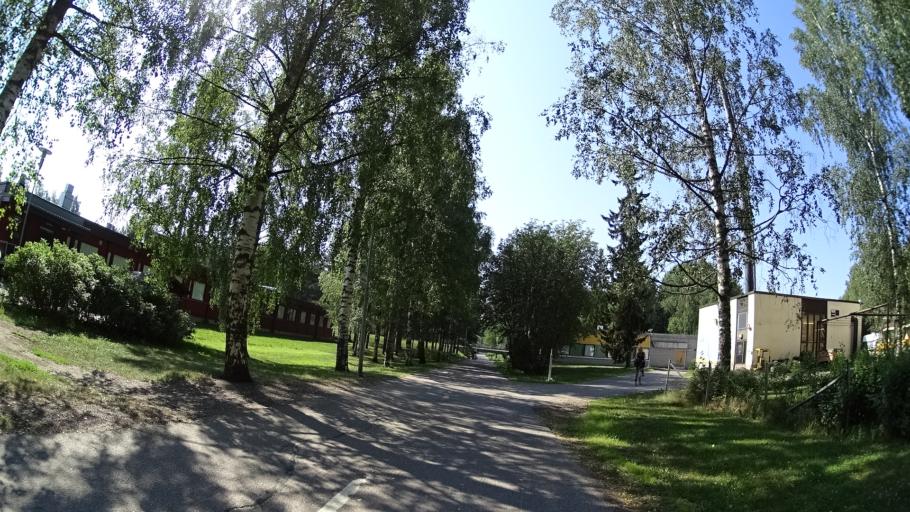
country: FI
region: Uusimaa
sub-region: Helsinki
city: Kerava
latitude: 60.3916
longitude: 25.0942
